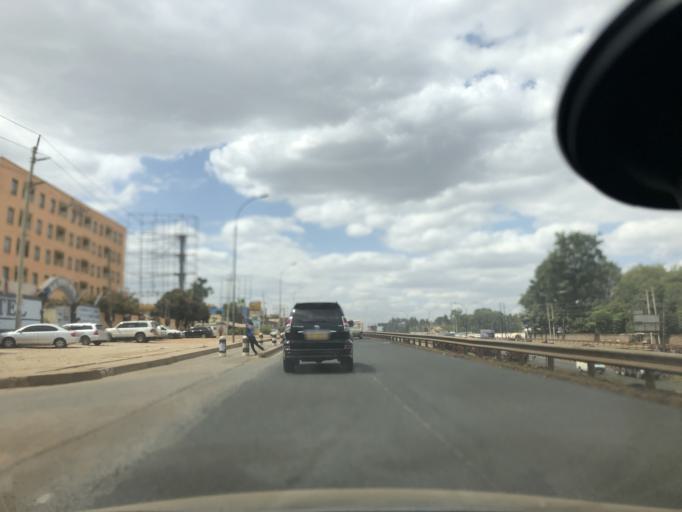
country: KE
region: Nairobi Area
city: Pumwani
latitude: -1.2327
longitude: 36.8754
